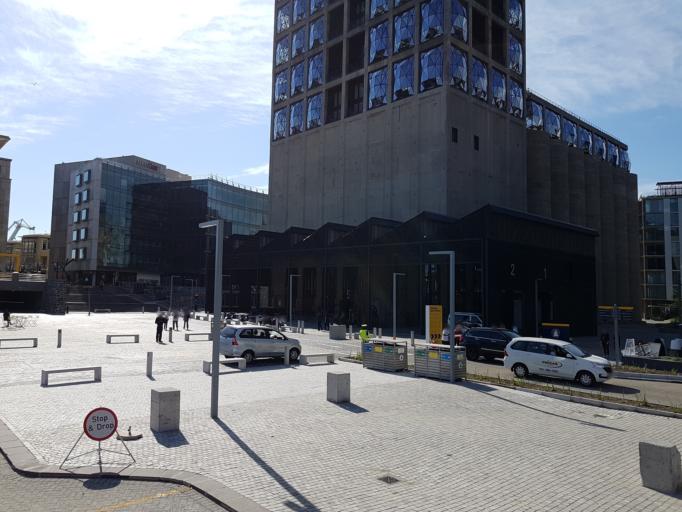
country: ZA
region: Western Cape
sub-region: City of Cape Town
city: Cape Town
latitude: -33.9089
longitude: 18.4222
